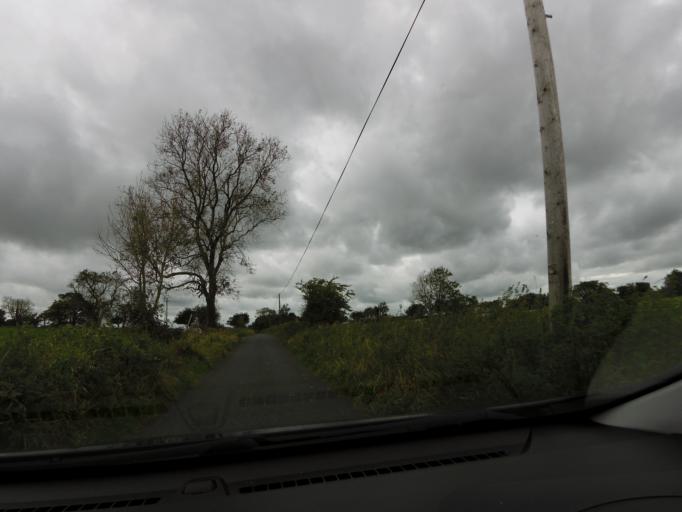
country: IE
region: Connaught
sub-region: County Galway
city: Athenry
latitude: 53.3238
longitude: -8.7343
